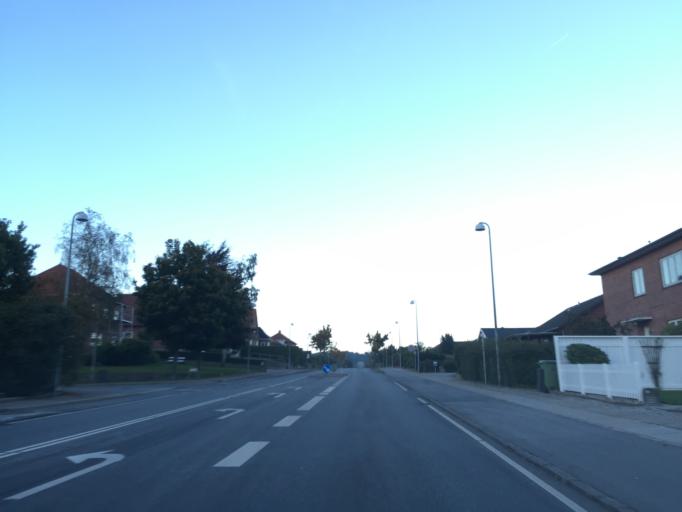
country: DK
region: South Denmark
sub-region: Aabenraa Kommune
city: Aabenraa
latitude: 55.0567
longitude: 9.4290
